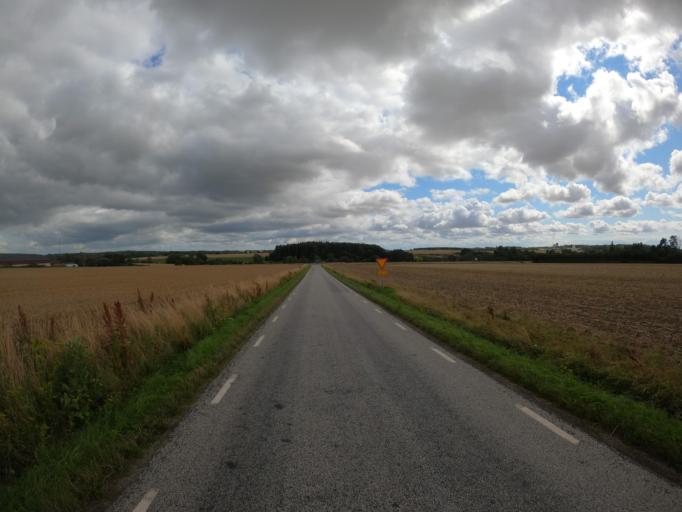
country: SE
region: Skane
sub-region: Lunds Kommun
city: Lund
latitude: 55.7167
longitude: 13.3018
